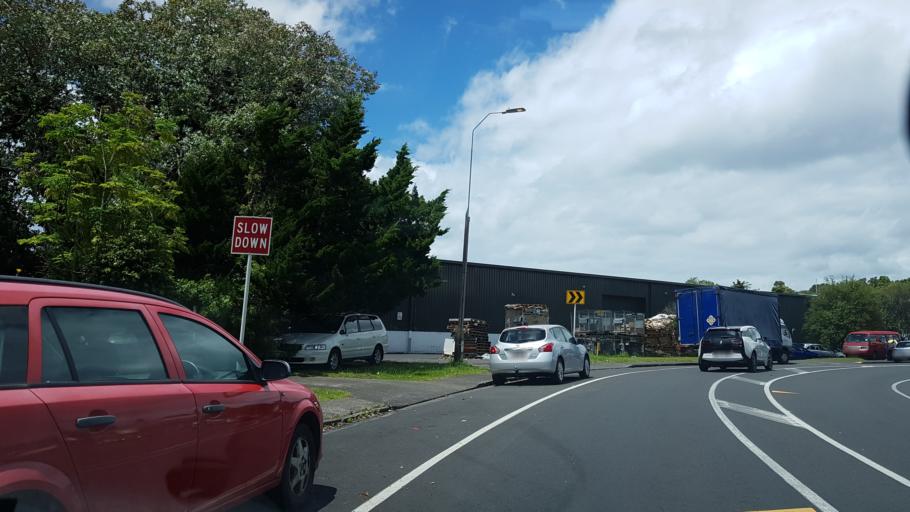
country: NZ
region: Auckland
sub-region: Auckland
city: North Shore
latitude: -36.7772
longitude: 174.7329
